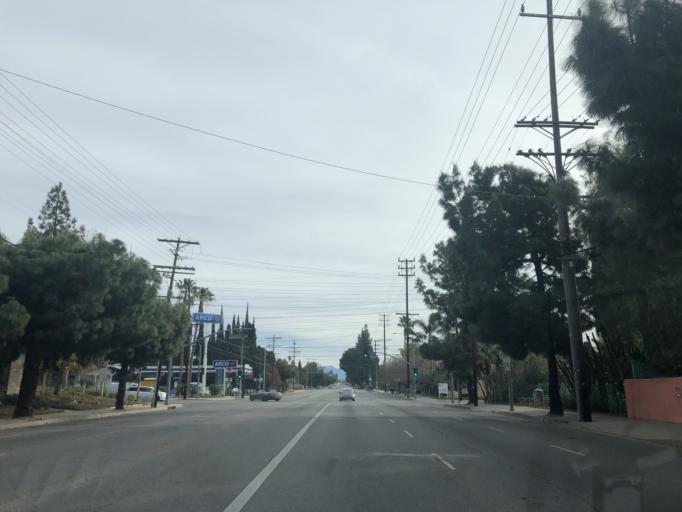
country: US
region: California
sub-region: Los Angeles County
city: Northridge
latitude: 34.2354
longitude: -118.5458
